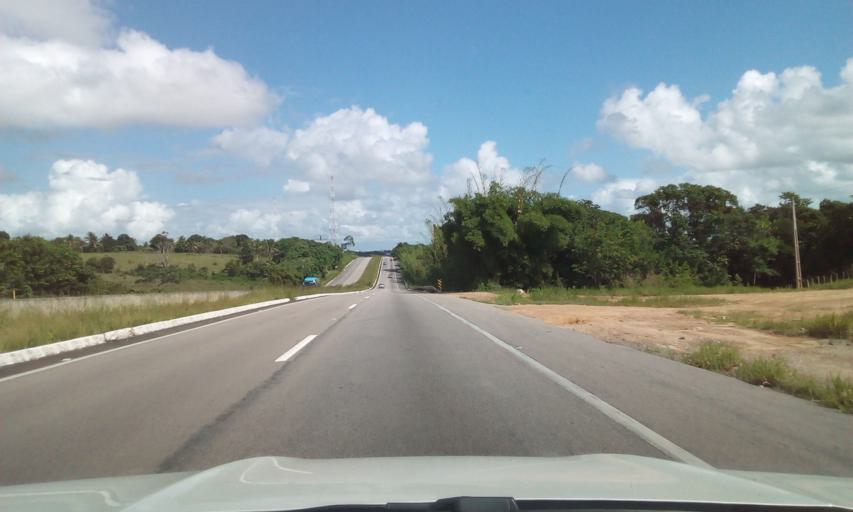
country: BR
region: Paraiba
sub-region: Conde
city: Conde
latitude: -7.3197
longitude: -34.9468
